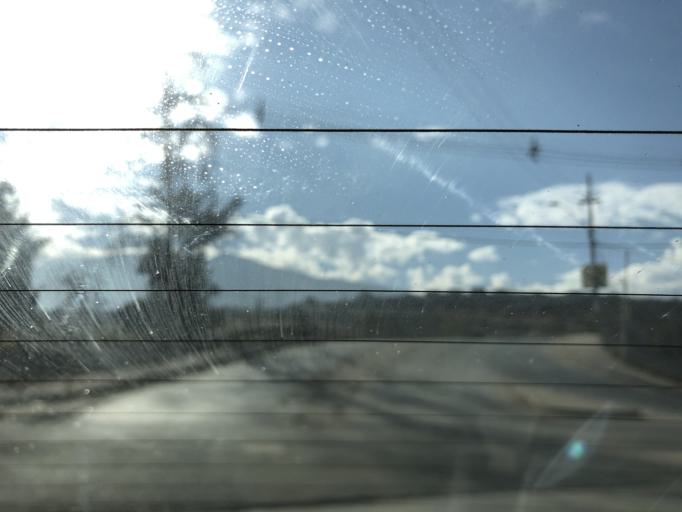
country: CL
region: Santiago Metropolitan
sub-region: Provincia de Cordillera
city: Puente Alto
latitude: -33.5890
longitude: -70.5372
